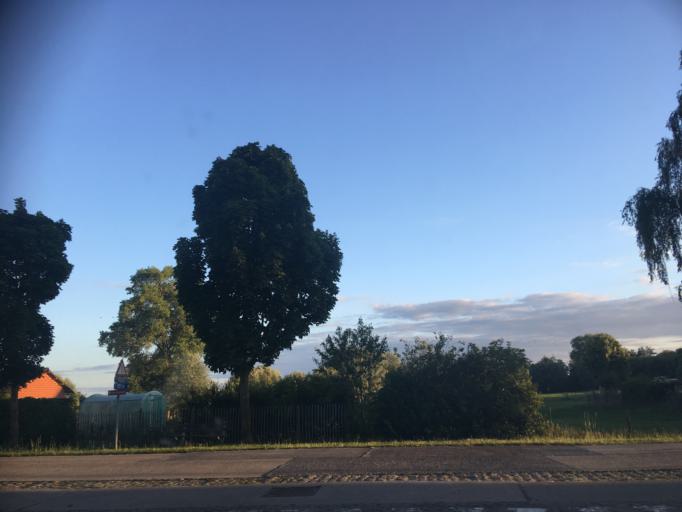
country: BE
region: Flanders
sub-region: Provincie West-Vlaanderen
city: Ieper
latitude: 50.8167
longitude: 2.8791
